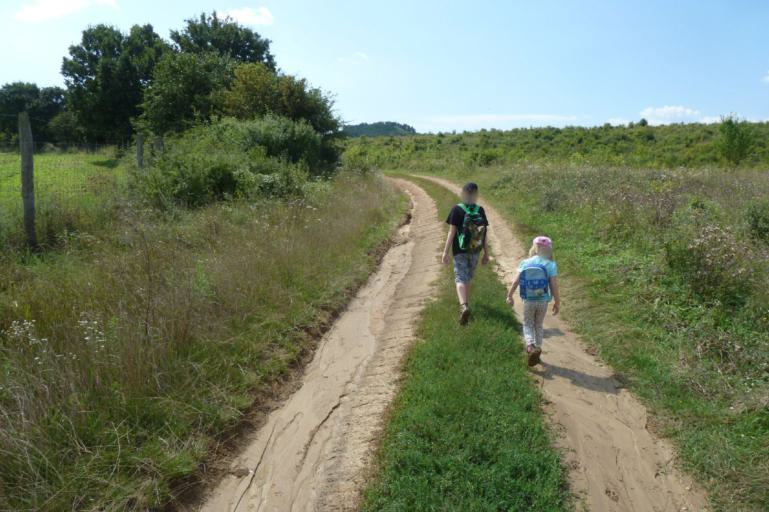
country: HU
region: Pest
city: Acsa
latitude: 47.8373
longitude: 19.3057
